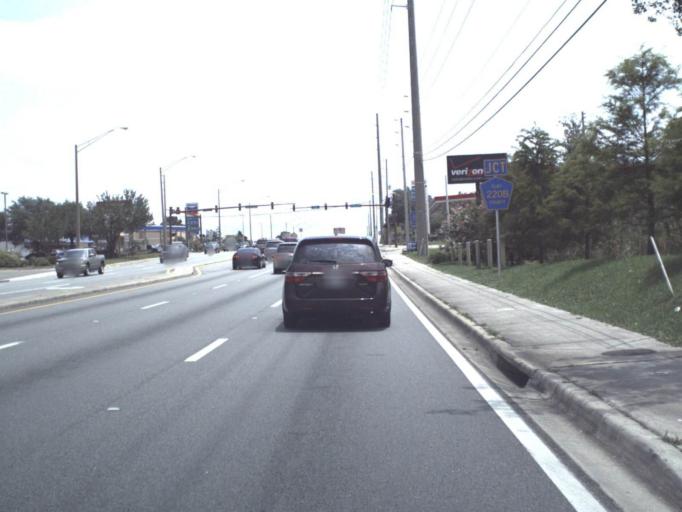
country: US
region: Florida
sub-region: Clay County
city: Lakeside
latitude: 30.1229
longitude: -81.7987
